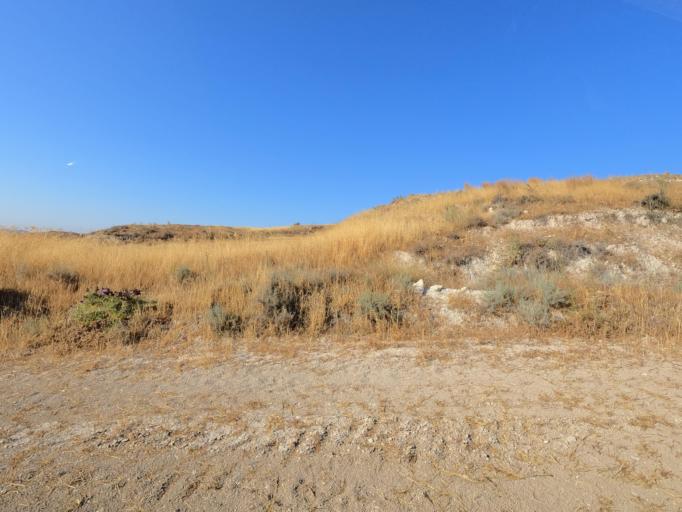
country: CY
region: Larnaka
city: Troulloi
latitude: 35.0244
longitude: 33.5759
